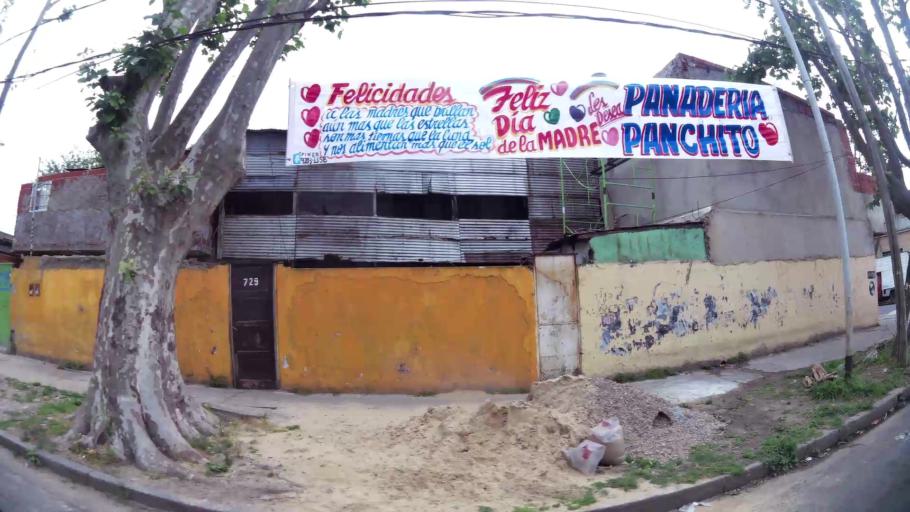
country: AR
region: Buenos Aires
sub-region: Partido de Avellaneda
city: Avellaneda
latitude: -34.6554
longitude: -58.3553
